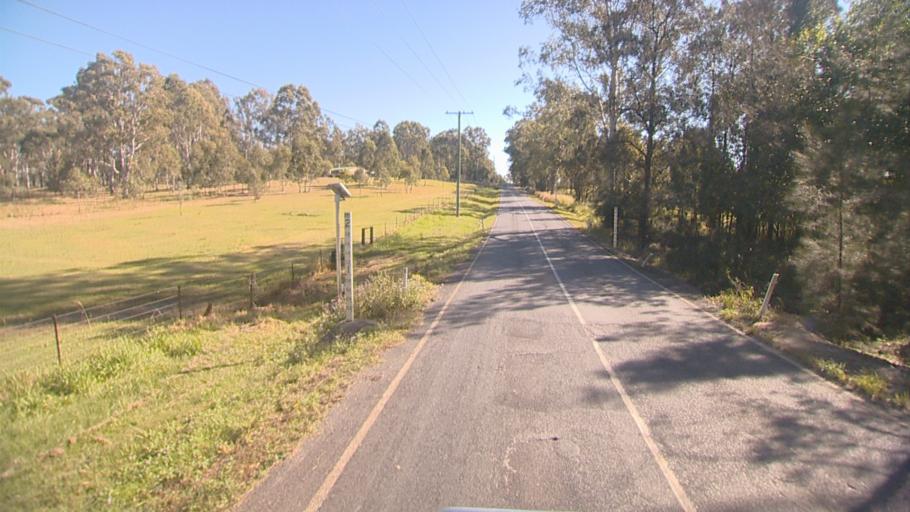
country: AU
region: Queensland
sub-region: Logan
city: Waterford West
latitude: -27.7168
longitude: 153.1338
